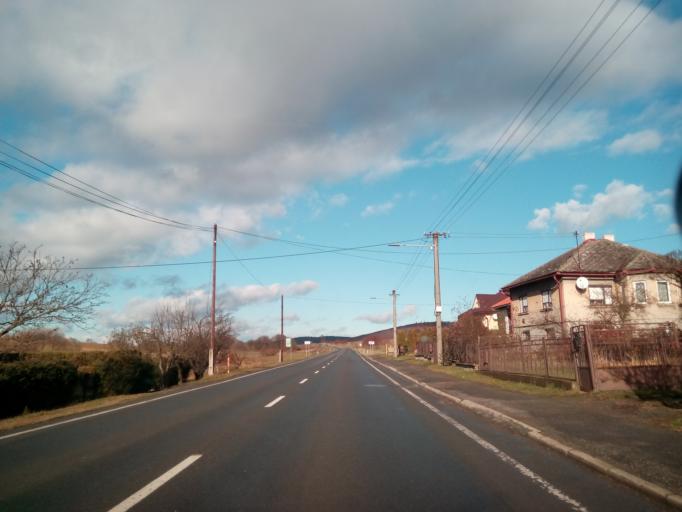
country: SK
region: Presovsky
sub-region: Okres Bardejov
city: Bardejov
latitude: 49.2200
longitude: 21.2935
